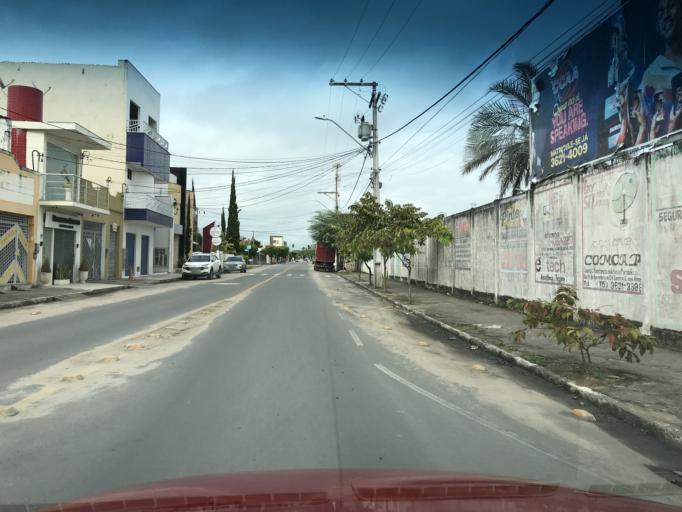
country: BR
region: Bahia
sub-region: Cruz Das Almas
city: Cruz das Almas
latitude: -12.6702
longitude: -39.1026
